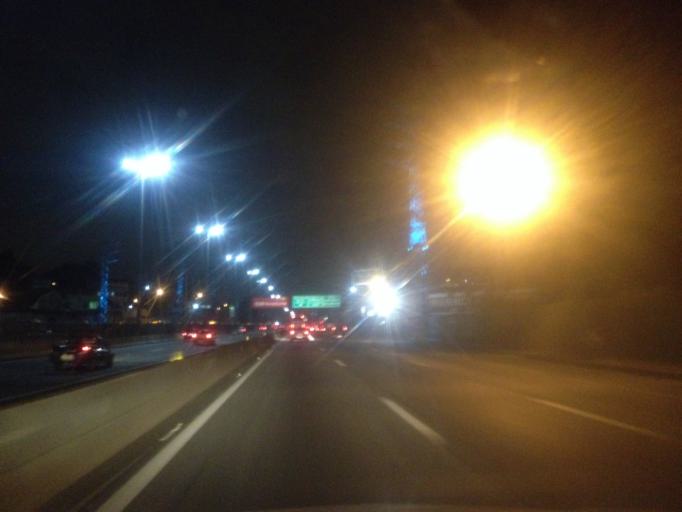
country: BR
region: Rio de Janeiro
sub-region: Sao Joao De Meriti
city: Sao Joao de Meriti
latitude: -22.7973
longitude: -43.3586
